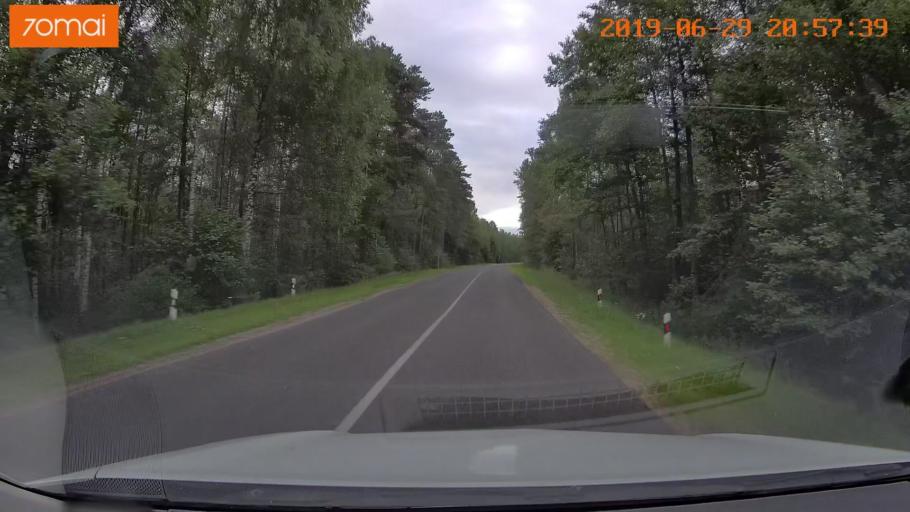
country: BY
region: Brest
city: Hantsavichy
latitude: 52.7218
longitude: 26.3729
